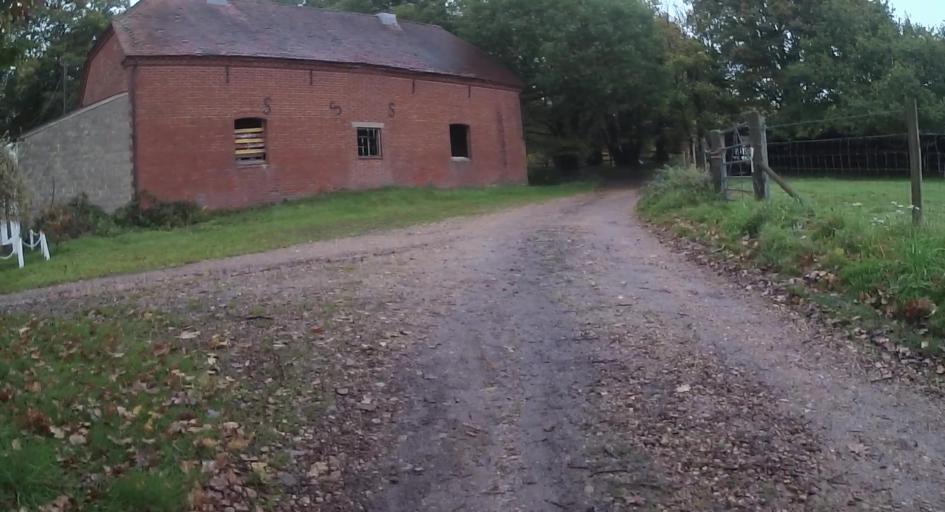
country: GB
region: England
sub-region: Surrey
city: Farnham
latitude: 51.2286
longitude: -0.8145
